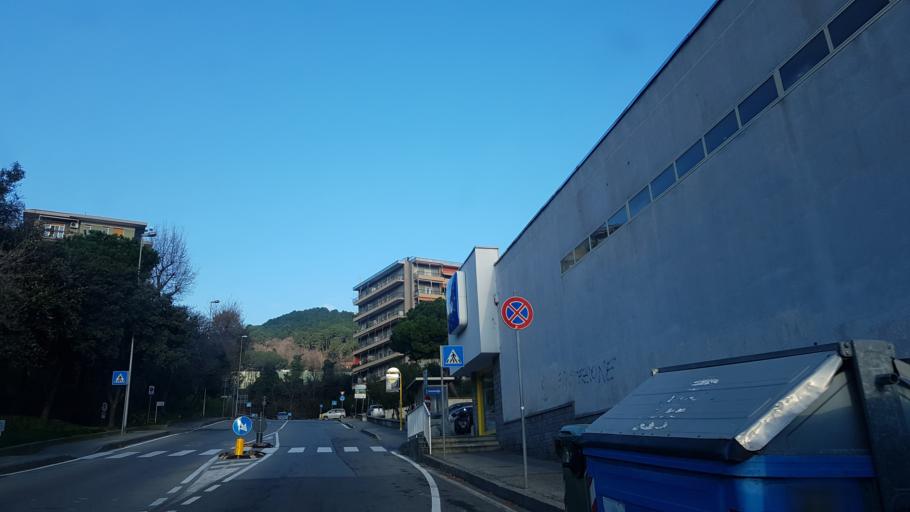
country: IT
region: Liguria
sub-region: Provincia di Savona
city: Savona
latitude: 44.3059
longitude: 8.4663
